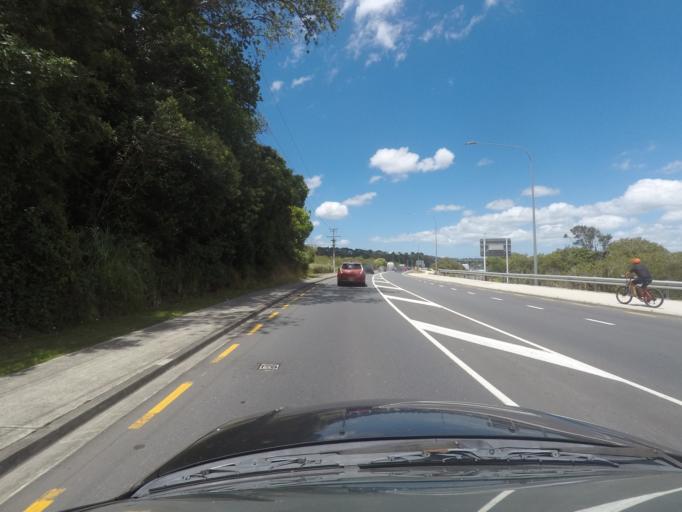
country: NZ
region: Northland
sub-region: Whangarei
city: Whangarei
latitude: -35.7311
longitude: 174.3435
